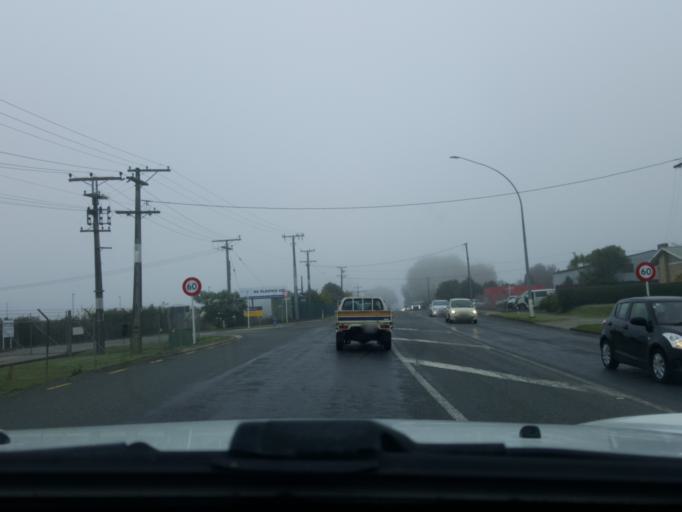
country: NZ
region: Waikato
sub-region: Waikato District
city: Ngaruawahia
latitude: -37.7016
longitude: 175.1990
